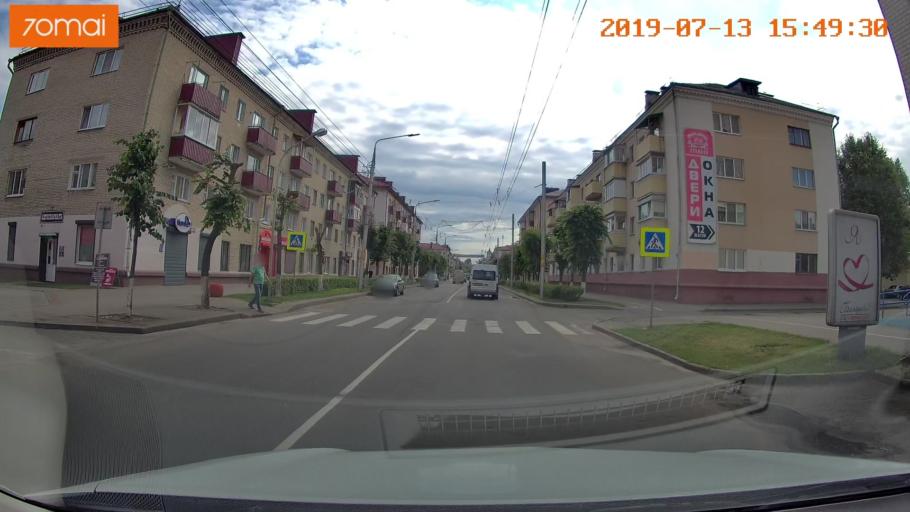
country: BY
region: Mogilev
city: Babruysk
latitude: 53.1466
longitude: 29.2287
